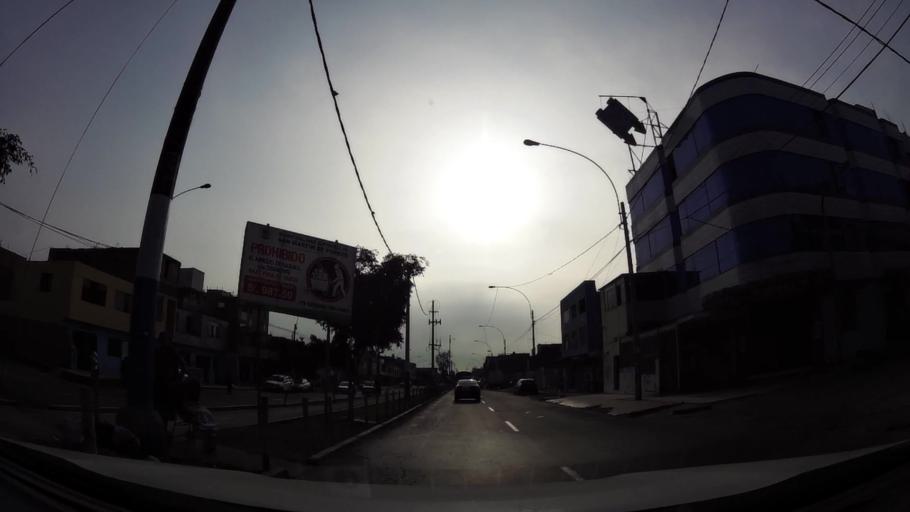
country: PE
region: Lima
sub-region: Lima
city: Independencia
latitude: -12.0240
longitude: -77.0806
